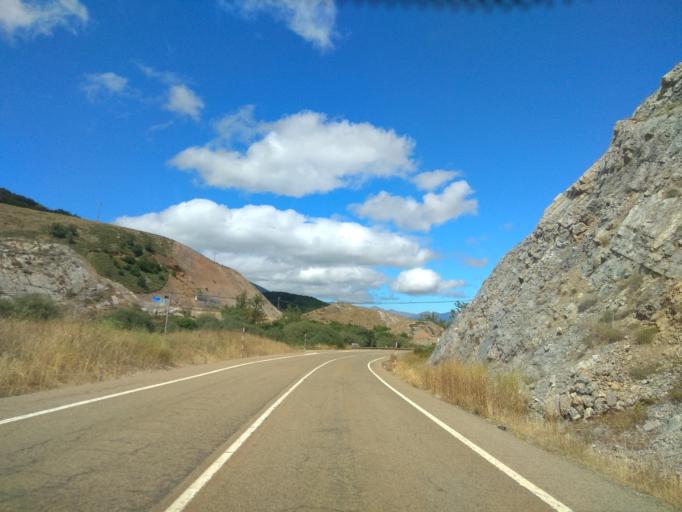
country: ES
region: Cantabria
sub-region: Provincia de Cantabria
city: Villaescusa
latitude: 42.9483
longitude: -4.1336
